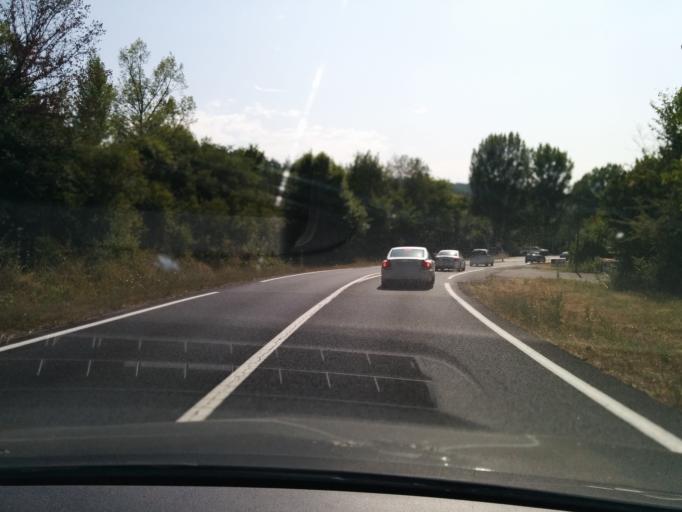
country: FR
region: Midi-Pyrenees
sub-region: Departement du Tarn
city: Cordes-sur-Ciel
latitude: 44.0587
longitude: 1.9699
